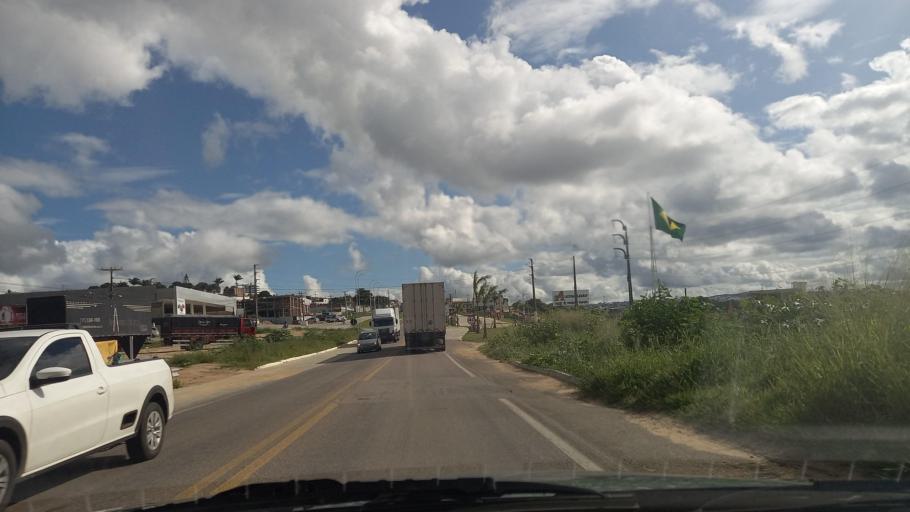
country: BR
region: Pernambuco
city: Garanhuns
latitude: -8.8711
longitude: -36.4654
